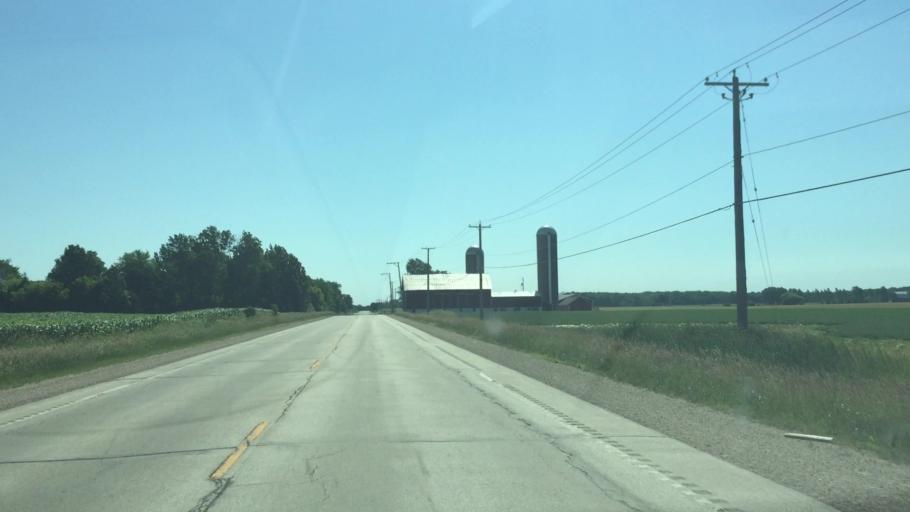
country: US
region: Wisconsin
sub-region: Calumet County
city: Hilbert
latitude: 44.1403
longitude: -88.1948
